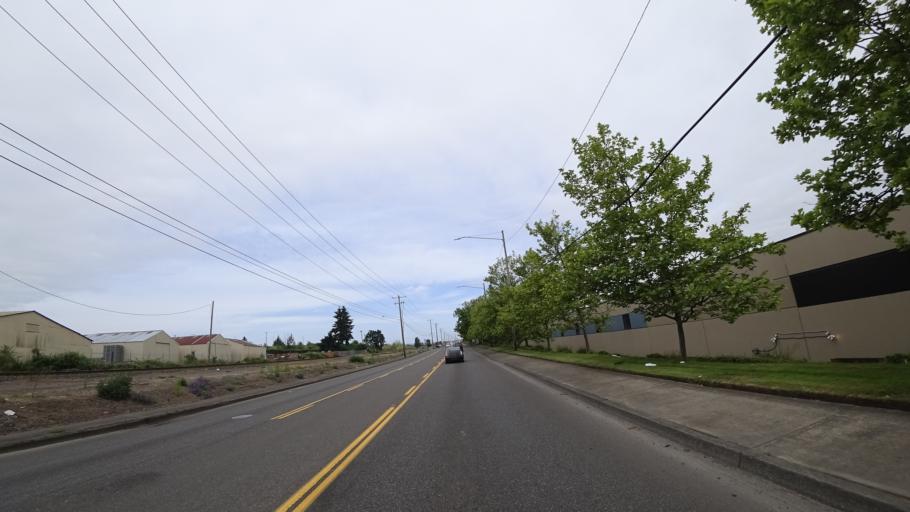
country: US
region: Oregon
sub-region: Multnomah County
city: Lents
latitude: 45.5653
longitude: -122.5811
